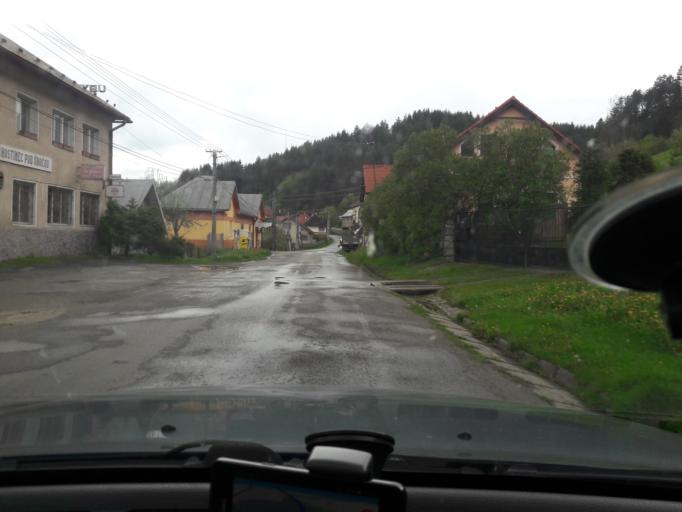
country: SK
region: Banskobystricky
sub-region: Okres Banska Bystrica
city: Brezno
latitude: 48.8150
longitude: 19.5760
